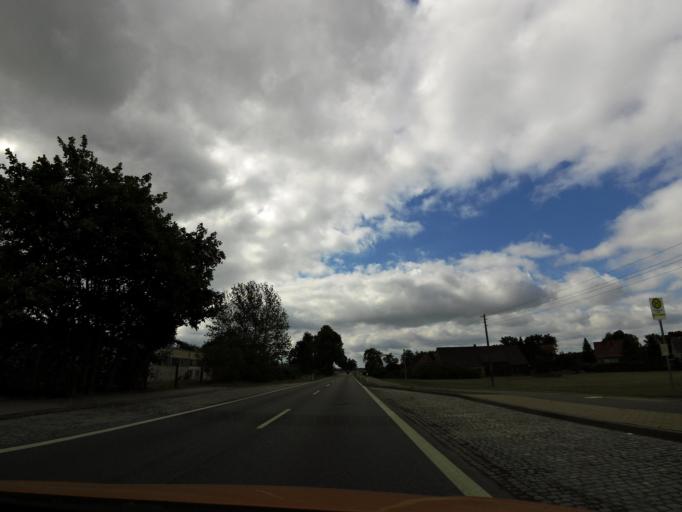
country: DE
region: Mecklenburg-Vorpommern
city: Muhl Rosin
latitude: 53.7286
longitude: 12.2764
